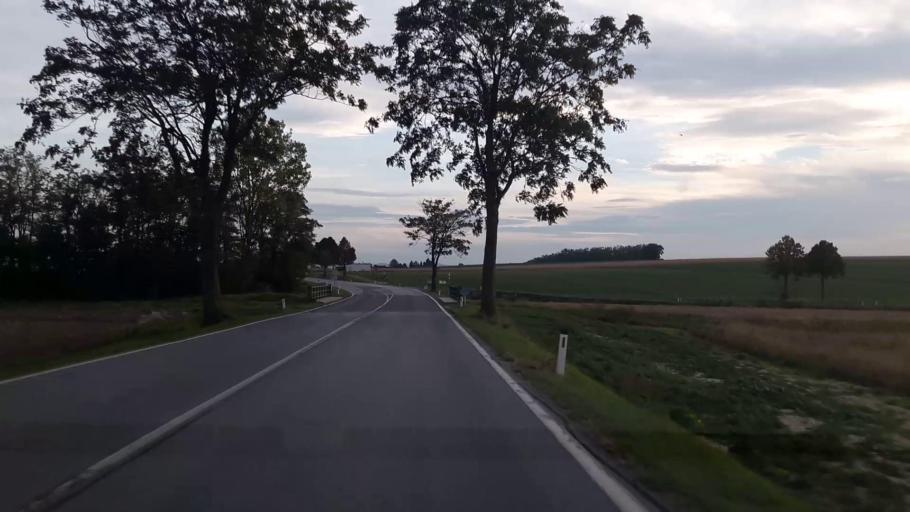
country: AT
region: Lower Austria
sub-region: Politischer Bezirk Korneuburg
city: Harmannsdorf
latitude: 48.4100
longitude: 16.3785
